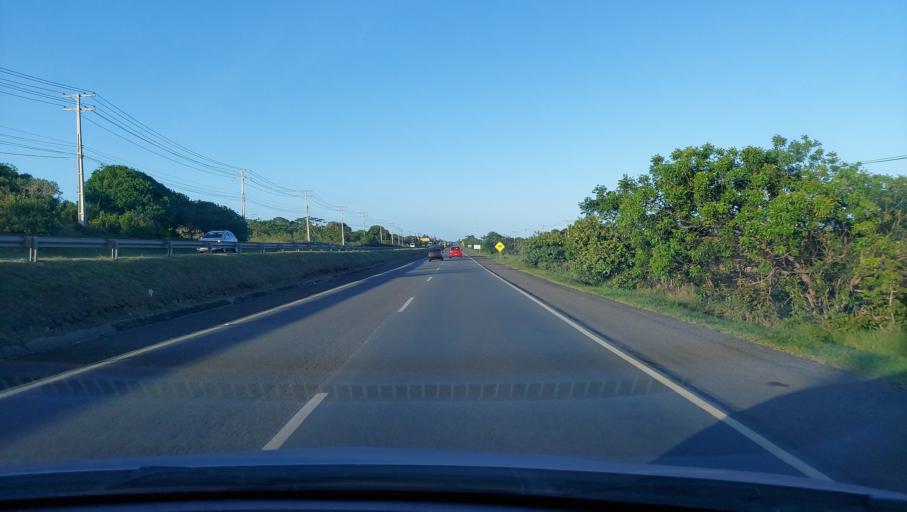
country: BR
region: Bahia
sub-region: Camacari
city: Camacari
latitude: -12.7905
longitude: -38.2065
